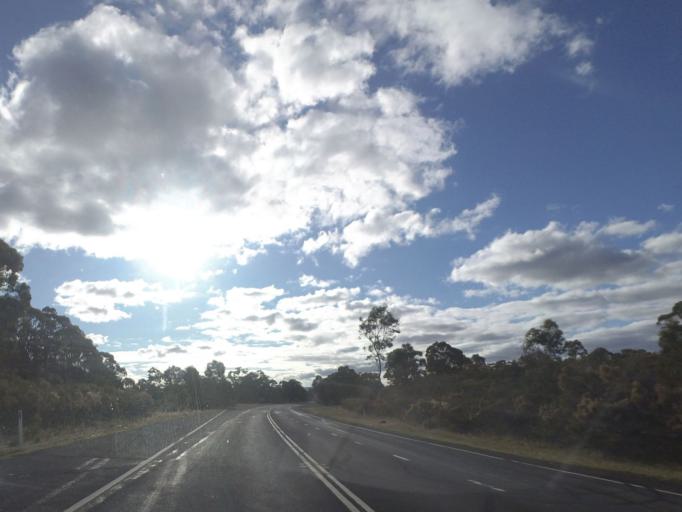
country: AU
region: Victoria
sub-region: Mount Alexander
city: Castlemaine
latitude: -37.1080
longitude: 144.3385
